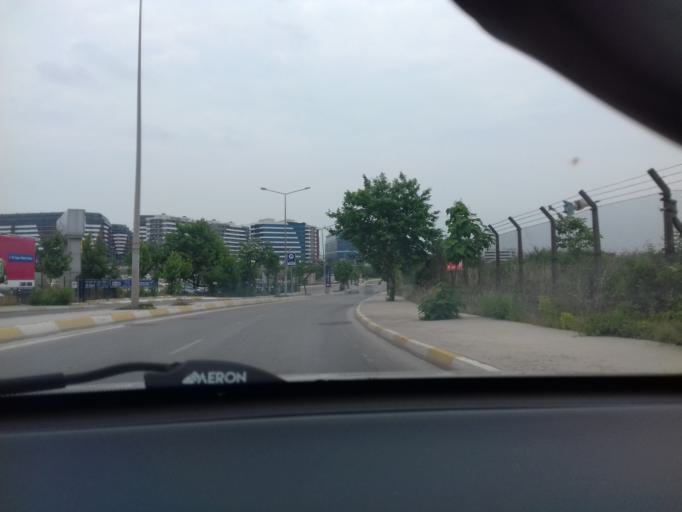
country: TR
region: Istanbul
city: Sultanbeyli
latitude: 40.9229
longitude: 29.3092
